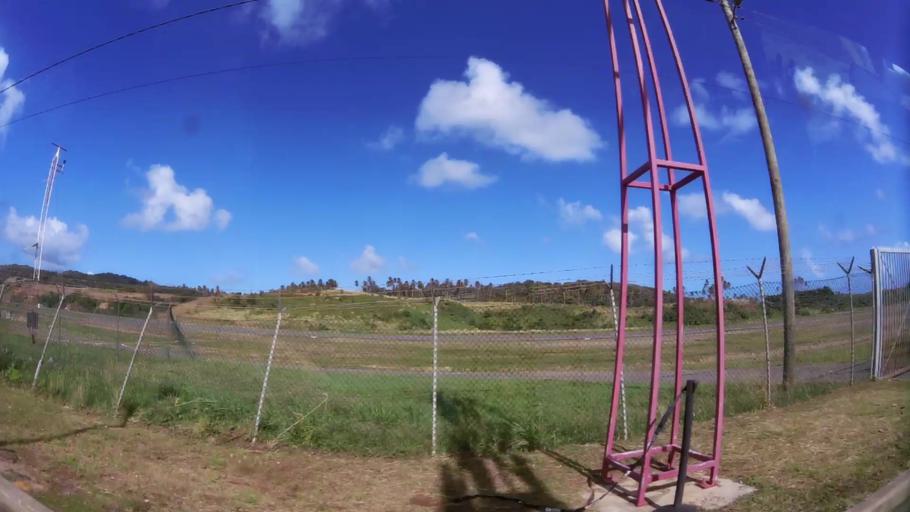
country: DM
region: Saint Andrew
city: Marigot
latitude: 15.5467
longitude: -61.2981
